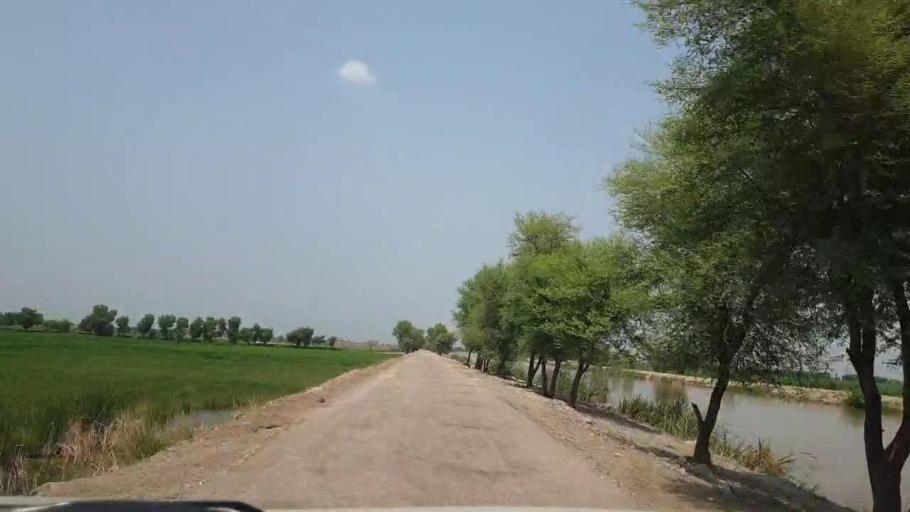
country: PK
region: Sindh
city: Dokri
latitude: 27.3316
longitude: 68.1096
